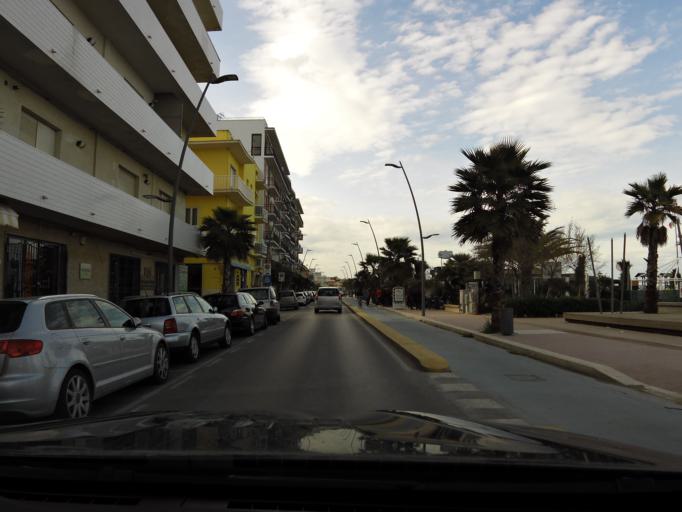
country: IT
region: The Marches
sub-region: Provincia di Macerata
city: Civitanova Marche
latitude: 43.3147
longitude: 13.7249
